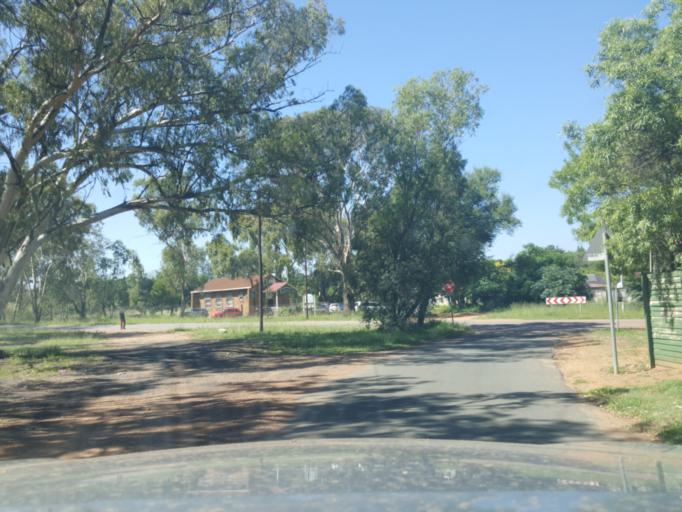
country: ZA
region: Gauteng
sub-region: City of Tshwane Metropolitan Municipality
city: Cullinan
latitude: -25.6782
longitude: 28.5244
